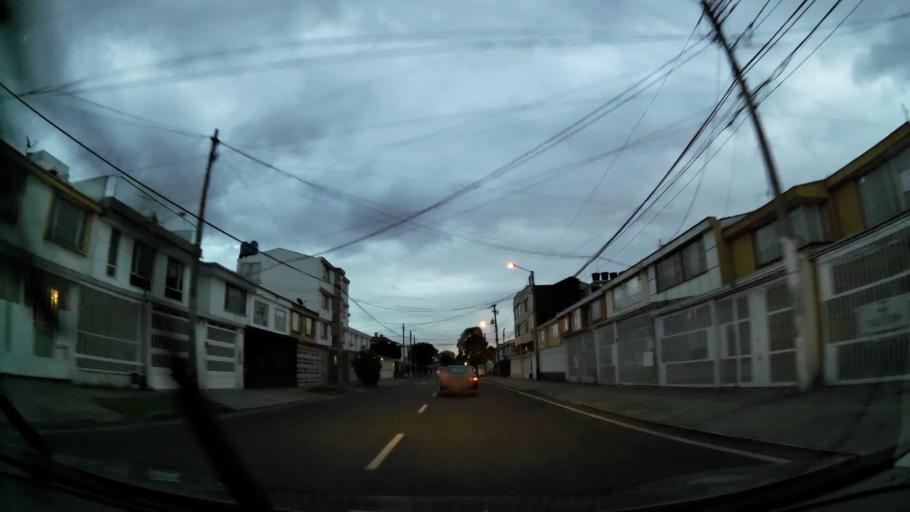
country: CO
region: Bogota D.C.
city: Bogota
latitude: 4.6707
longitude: -74.1091
